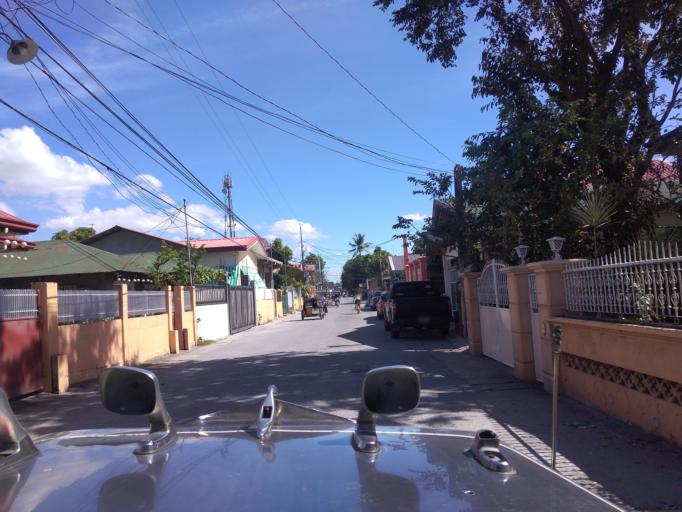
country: PH
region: Central Luzon
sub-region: Province of Pampanga
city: Santa Rita
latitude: 14.9951
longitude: 120.6124
